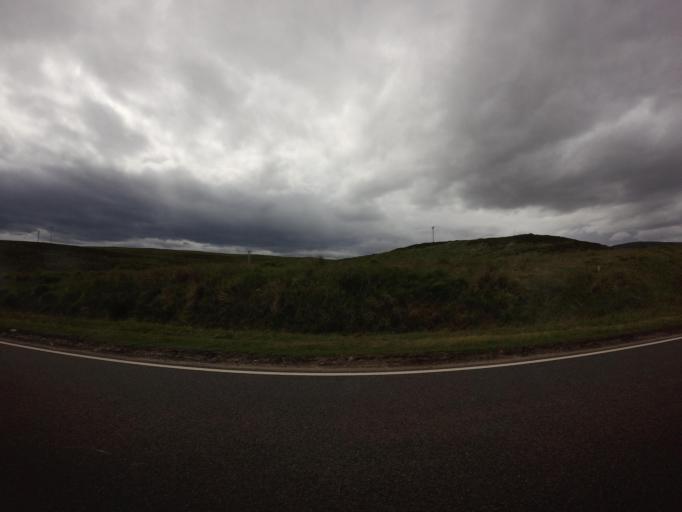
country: GB
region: Scotland
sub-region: Highland
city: Muir of Ord
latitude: 57.6922
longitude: -4.7613
